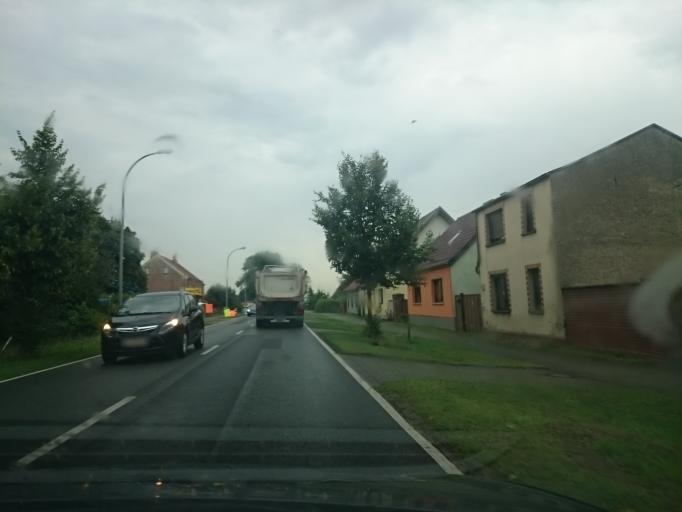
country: DE
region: Brandenburg
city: Oranienburg
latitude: 52.8494
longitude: 13.1756
